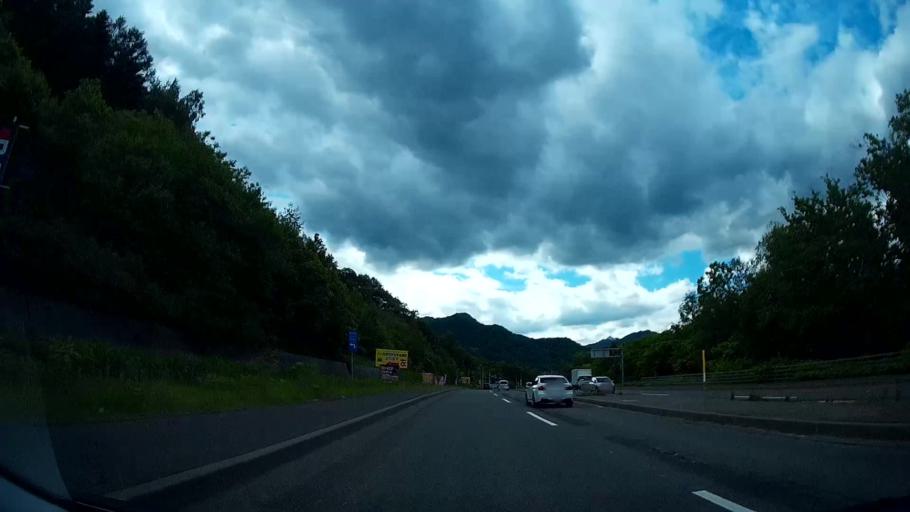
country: JP
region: Hokkaido
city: Sapporo
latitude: 42.9570
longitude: 141.2330
